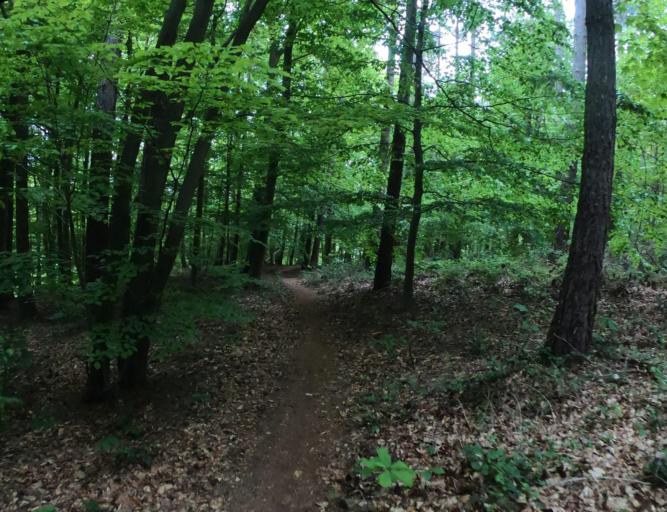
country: BE
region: Flanders
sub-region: Provincie Vlaams-Brabant
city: Beersel
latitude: 50.7383
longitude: 4.3070
